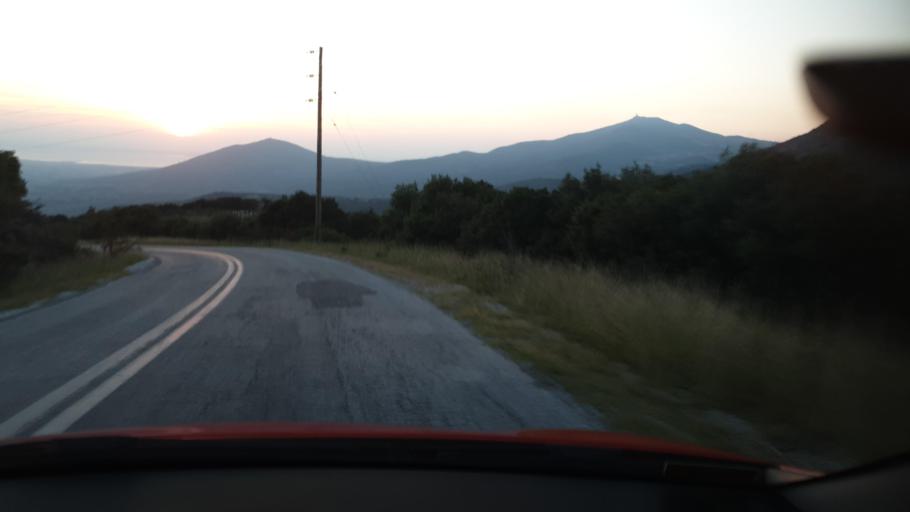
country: GR
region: Central Macedonia
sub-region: Nomos Thessalonikis
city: Peristera
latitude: 40.5238
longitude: 23.2001
